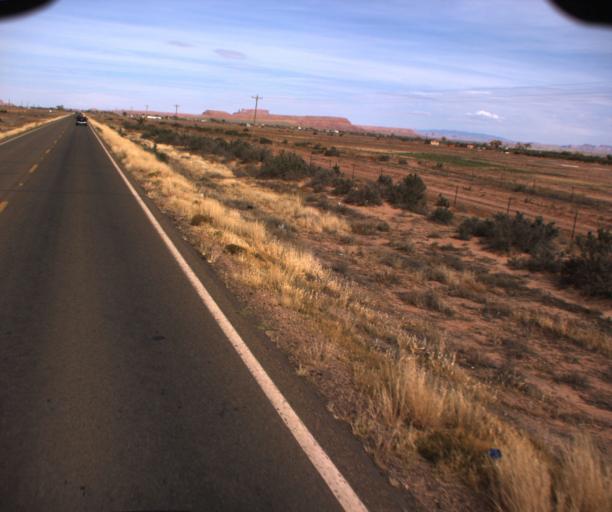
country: US
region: Arizona
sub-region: Apache County
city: Many Farms
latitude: 36.3861
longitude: -109.6109
